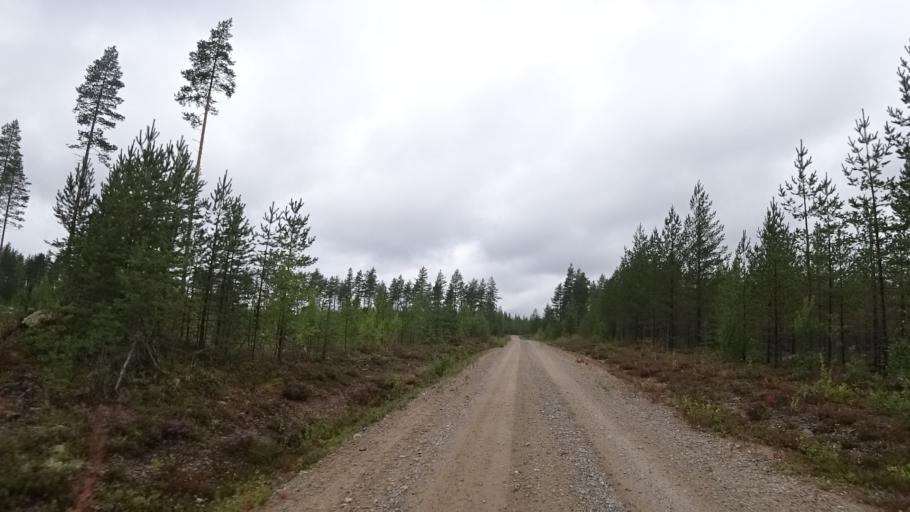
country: FI
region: North Karelia
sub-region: Pielisen Karjala
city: Lieksa
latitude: 63.5127
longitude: 30.1333
